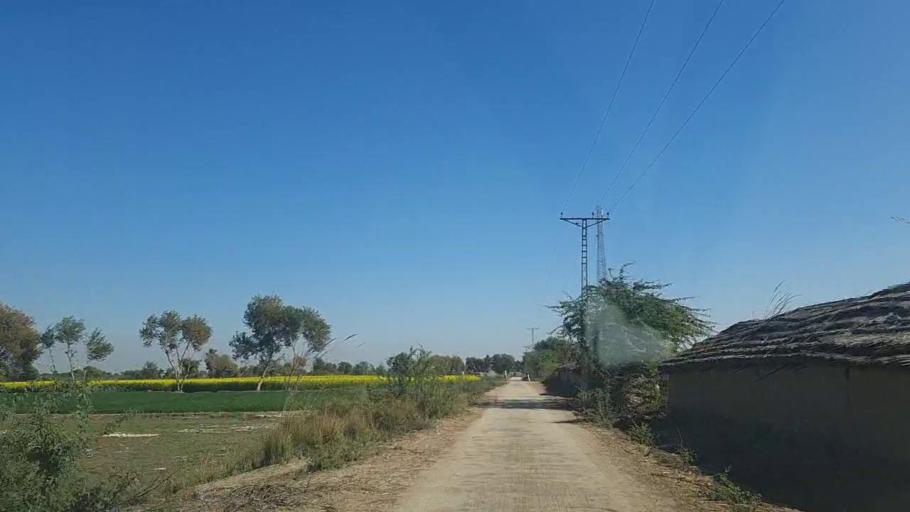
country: PK
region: Sindh
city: Khadro
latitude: 26.1774
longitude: 68.8264
